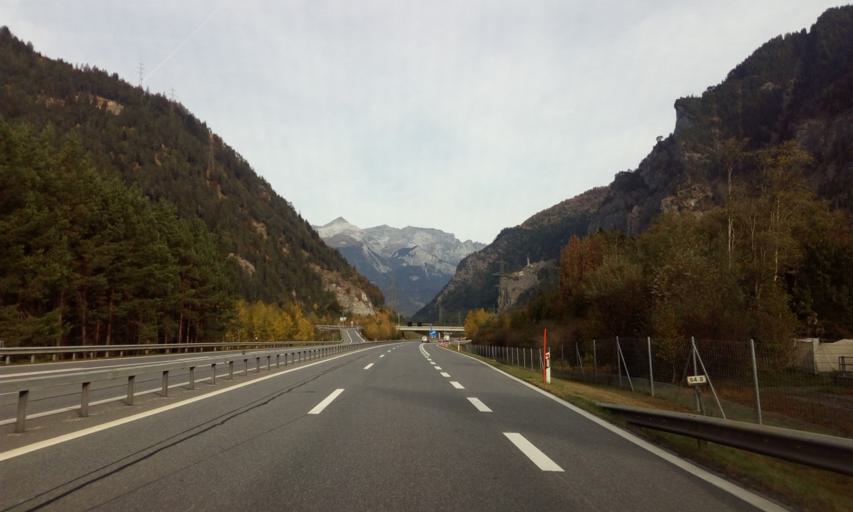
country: CH
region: Grisons
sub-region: Hinterrhein District
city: Cazis
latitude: 46.7614
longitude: 9.4235
